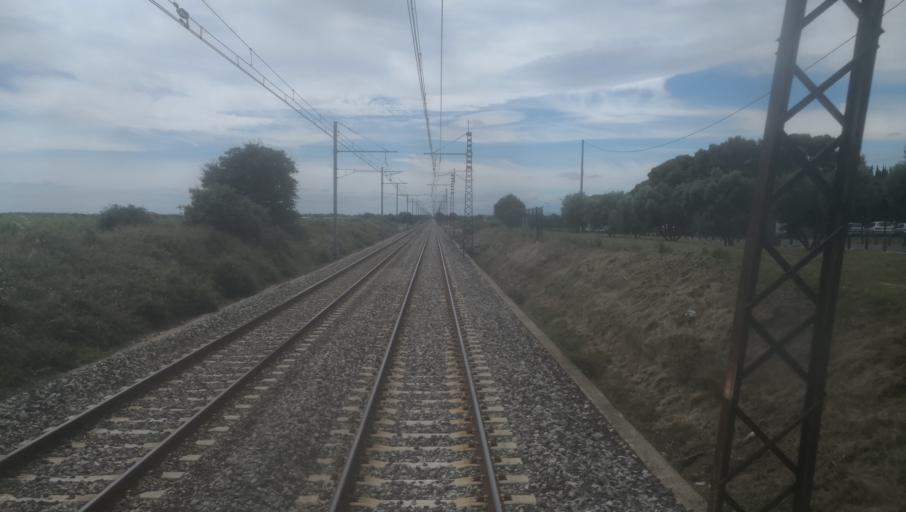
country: FR
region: Languedoc-Roussillon
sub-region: Departement de l'Herault
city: Portiragnes
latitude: 43.3198
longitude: 3.3552
